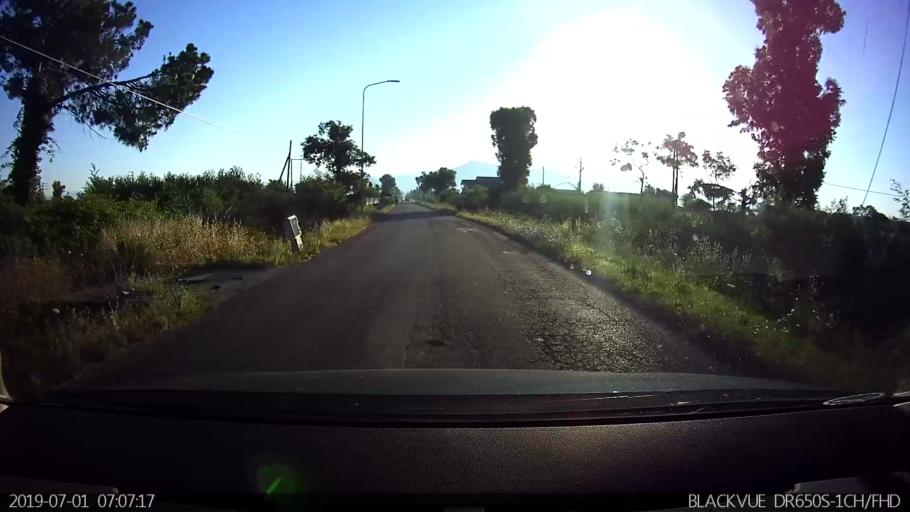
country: IT
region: Latium
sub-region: Provincia di Latina
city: Borgo Hermada
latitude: 41.2878
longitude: 13.1372
